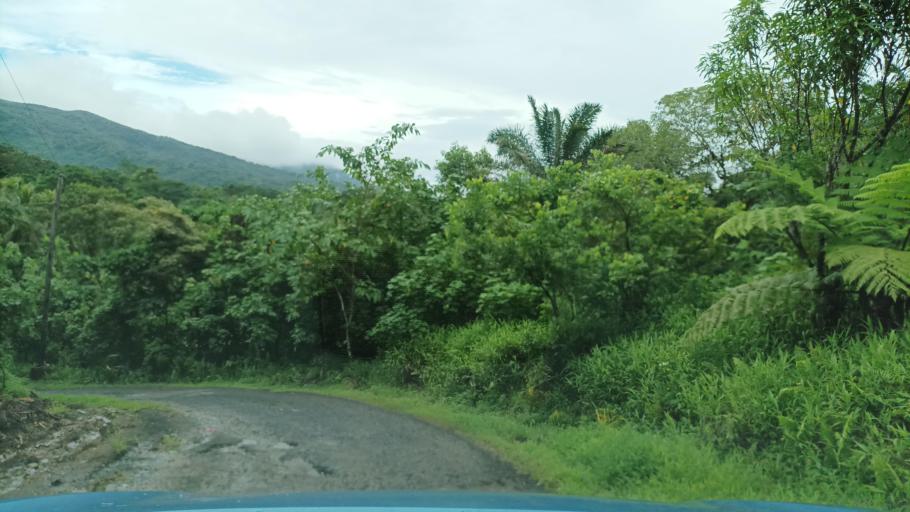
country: FM
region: Pohnpei
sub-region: Sokehs Municipality
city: Palikir - National Government Center
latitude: 6.8359
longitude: 158.1743
